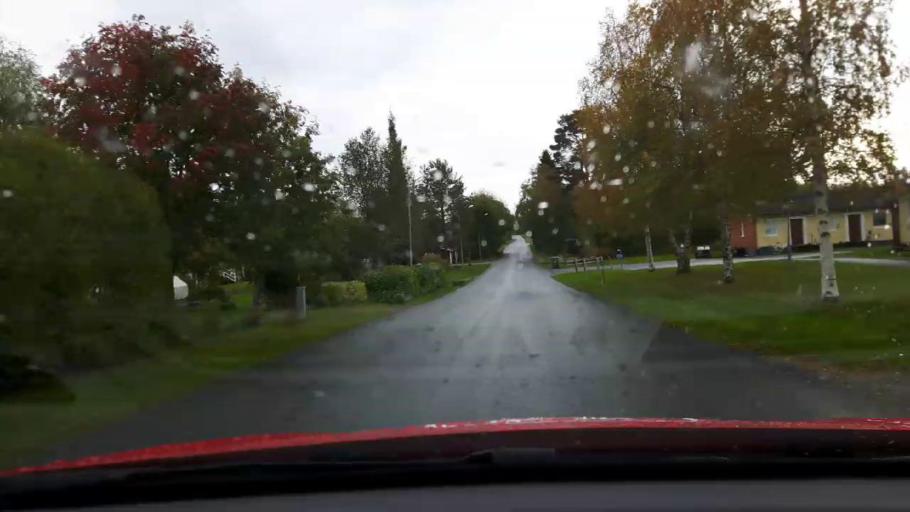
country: SE
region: Jaemtland
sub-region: Bergs Kommun
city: Hoverberg
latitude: 62.9279
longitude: 14.5160
